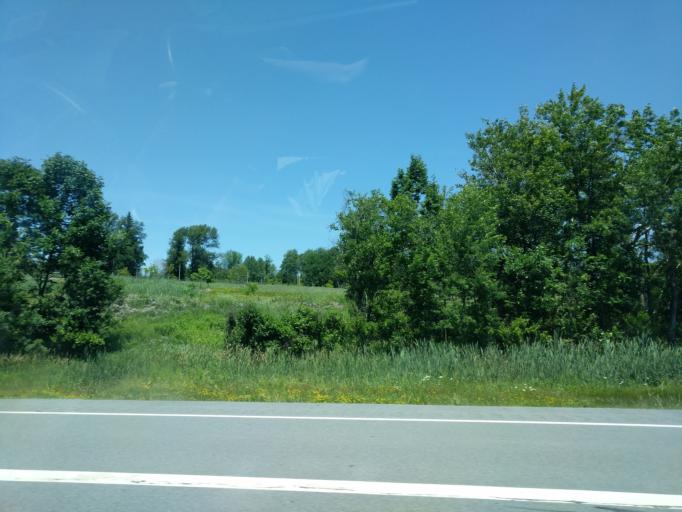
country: US
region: New York
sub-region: Sullivan County
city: Monticello
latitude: 41.6436
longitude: -74.6471
